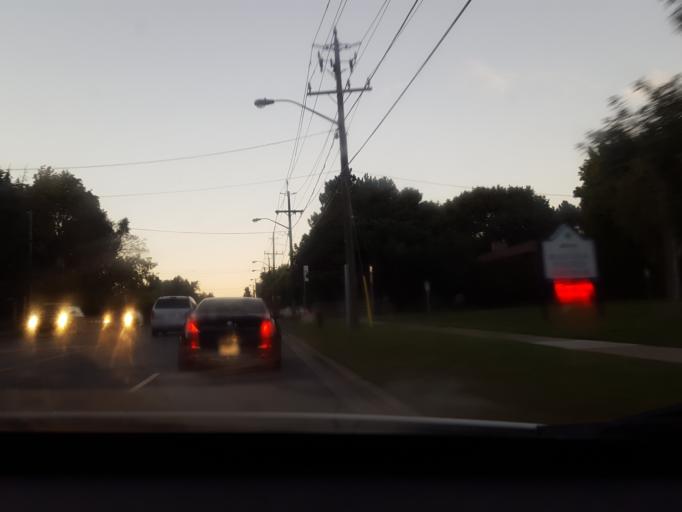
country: CA
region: Ontario
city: Willowdale
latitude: 43.7515
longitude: -79.3847
